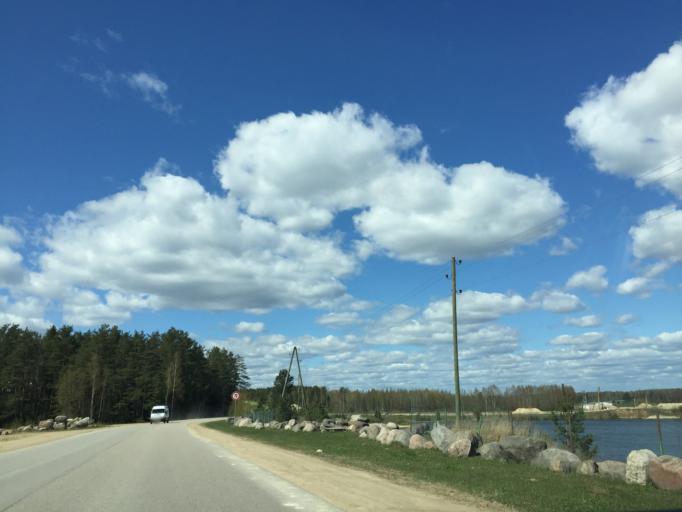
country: LV
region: Vilanu
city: Vilani
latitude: 56.5737
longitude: 27.0445
